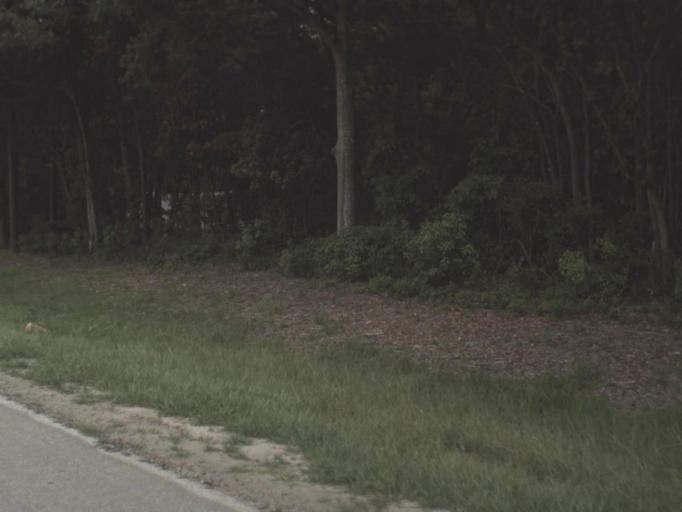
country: US
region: Florida
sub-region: Alachua County
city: Newberry
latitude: 29.7217
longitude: -82.6072
